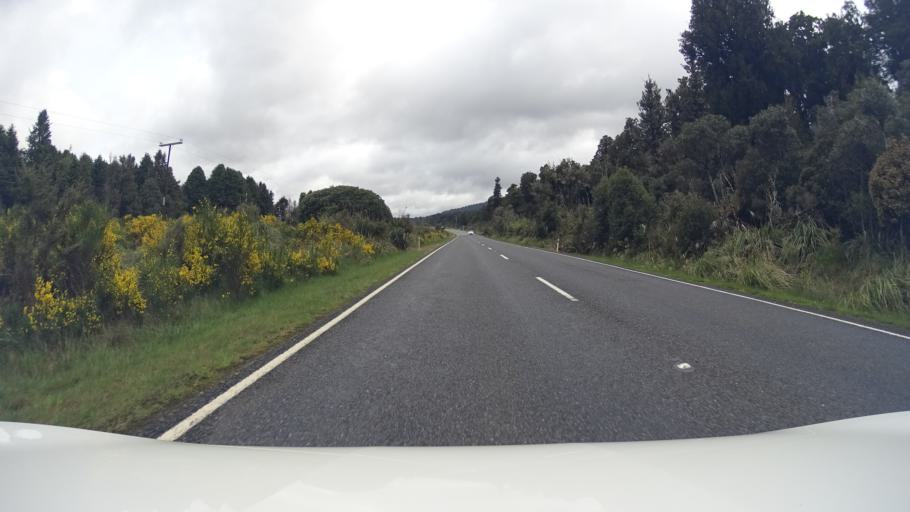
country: NZ
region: Manawatu-Wanganui
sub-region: Ruapehu District
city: Waiouru
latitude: -39.2453
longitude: 175.3900
